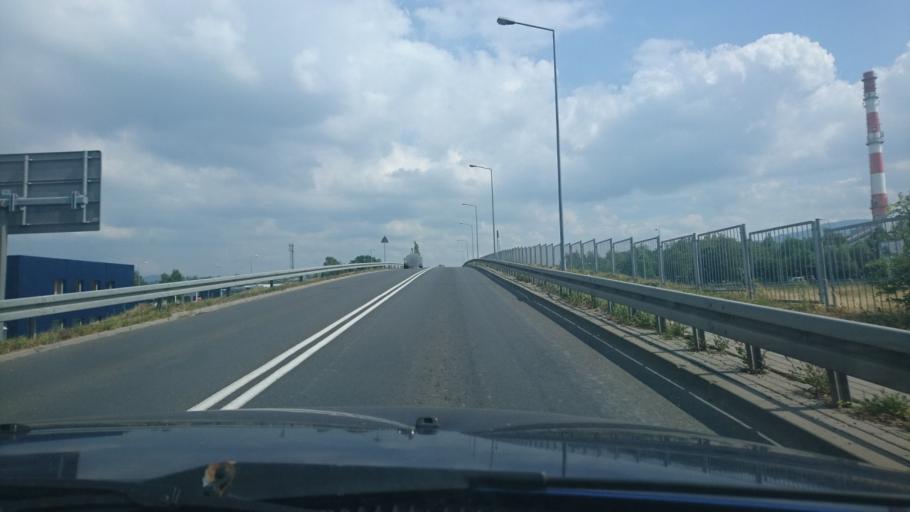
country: PL
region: Silesian Voivodeship
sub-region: Powiat bielski
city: Mazancowice
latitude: 49.8283
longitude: 18.9670
